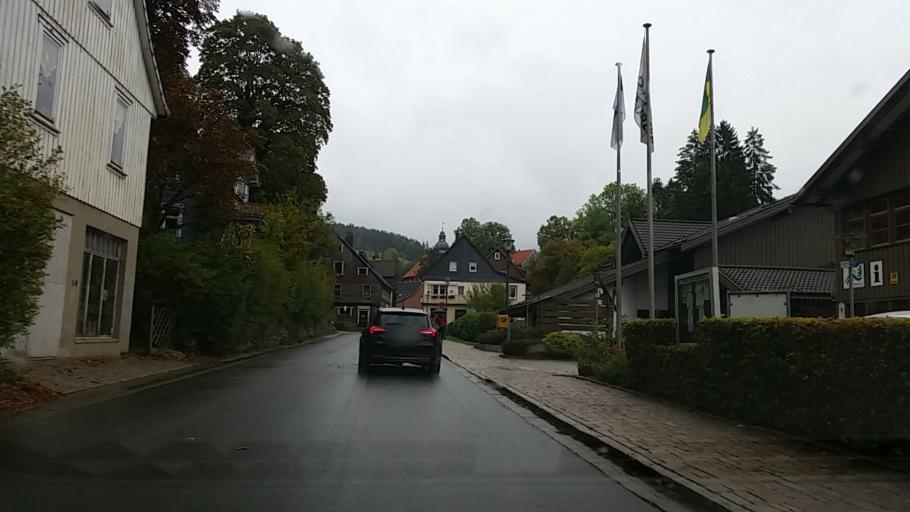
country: DE
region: Lower Saxony
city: Altenau
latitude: 51.8042
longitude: 10.4428
